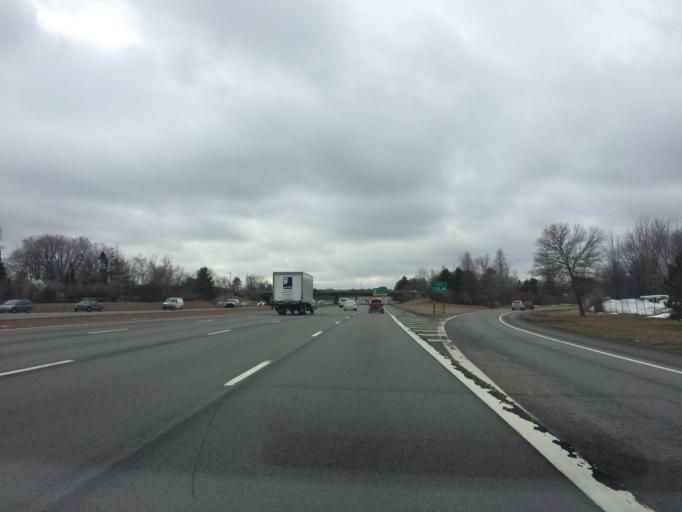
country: US
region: New York
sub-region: Monroe County
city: Rochester
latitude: 43.0982
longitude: -77.6011
